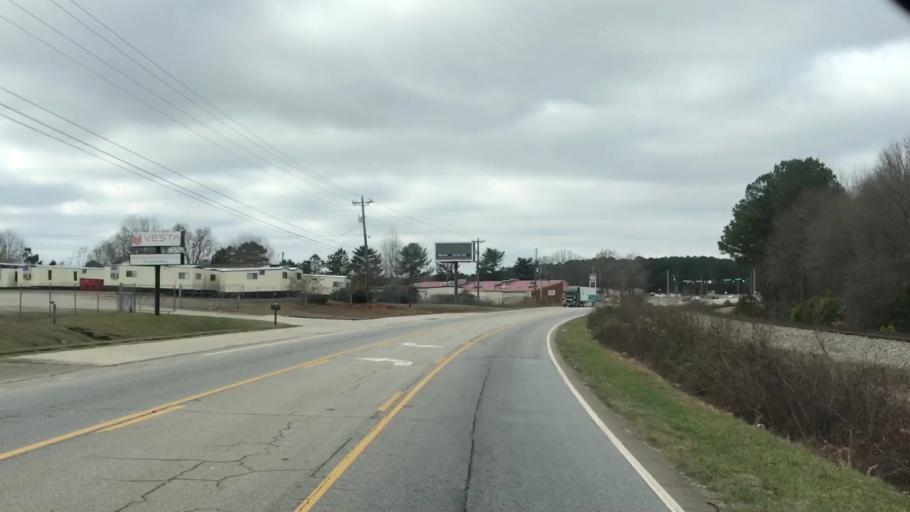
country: US
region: Georgia
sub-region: Barrow County
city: Russell
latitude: 33.9724
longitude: -83.6857
